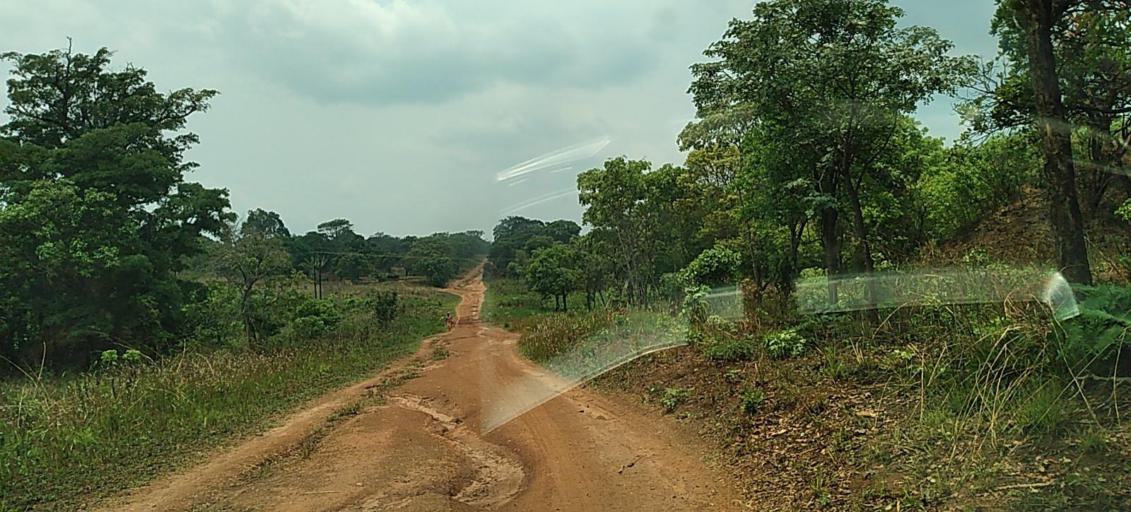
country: ZM
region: North-Western
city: Mwinilunga
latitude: -11.5371
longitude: 24.7830
